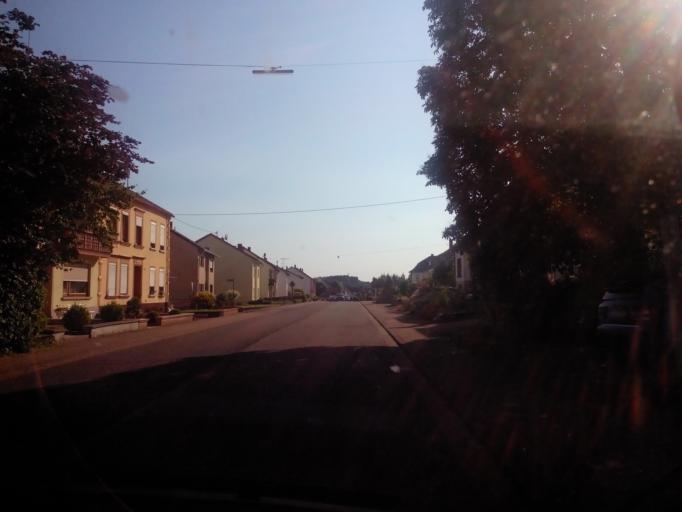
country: DE
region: Saarland
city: Nalbach
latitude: 49.4157
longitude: 6.7606
